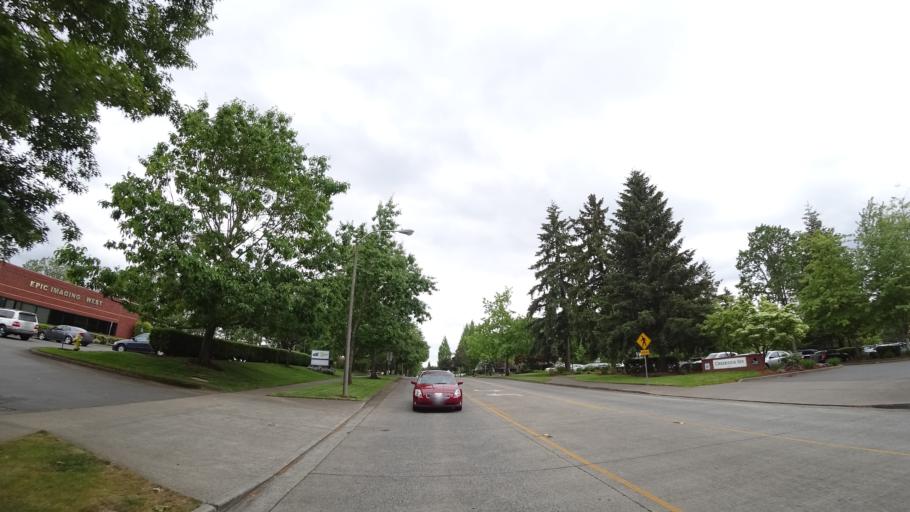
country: US
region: Oregon
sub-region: Washington County
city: Tigard
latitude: 45.4554
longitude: -122.7889
